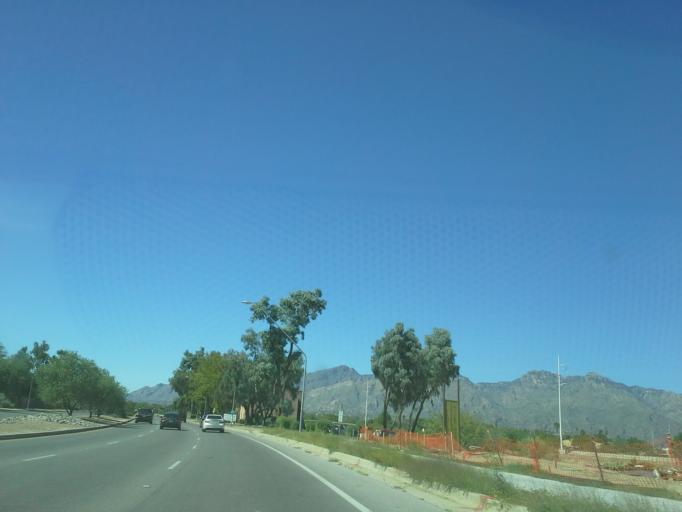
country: US
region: Arizona
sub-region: Pima County
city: Tucson
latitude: 32.2399
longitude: -110.8415
